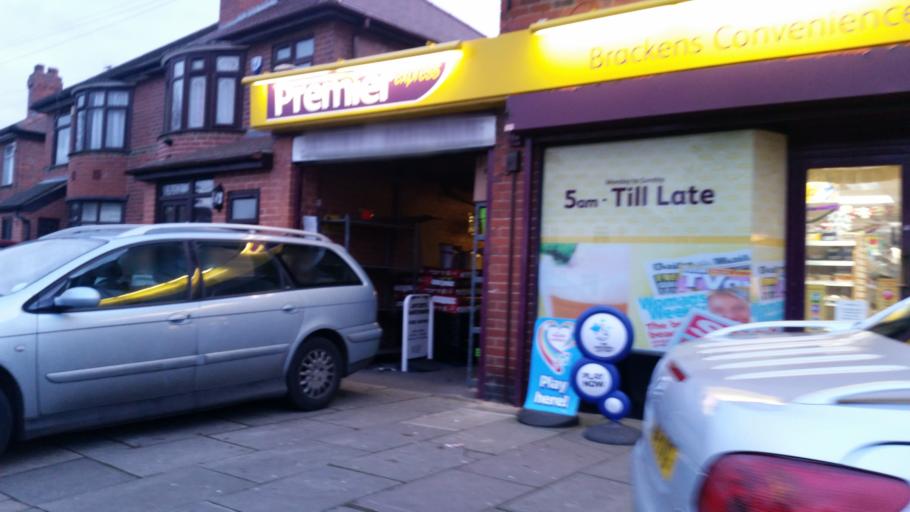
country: GB
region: England
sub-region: Derby
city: Derby
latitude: 52.8900
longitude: -1.4411
